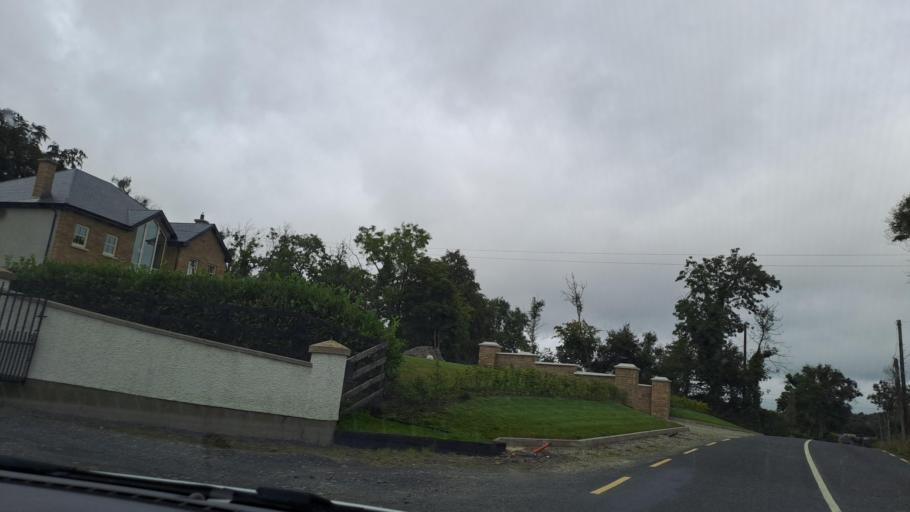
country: IE
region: Ulster
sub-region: County Monaghan
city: Carrickmacross
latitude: 54.0194
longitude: -6.7124
